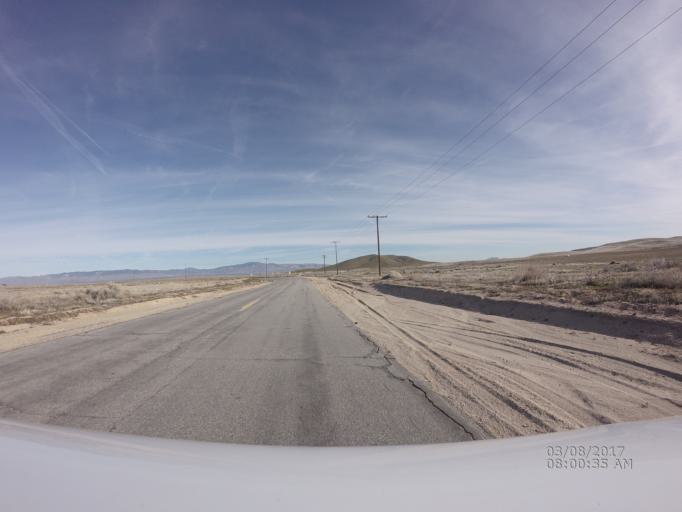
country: US
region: California
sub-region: Los Angeles County
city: Green Valley
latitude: 34.7281
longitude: -118.4141
